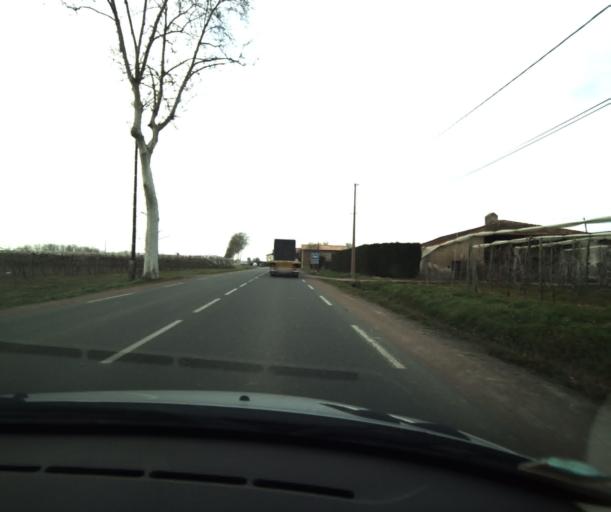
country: FR
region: Midi-Pyrenees
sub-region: Departement du Tarn-et-Garonne
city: Saint-Porquier
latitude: 44.0217
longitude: 1.1551
